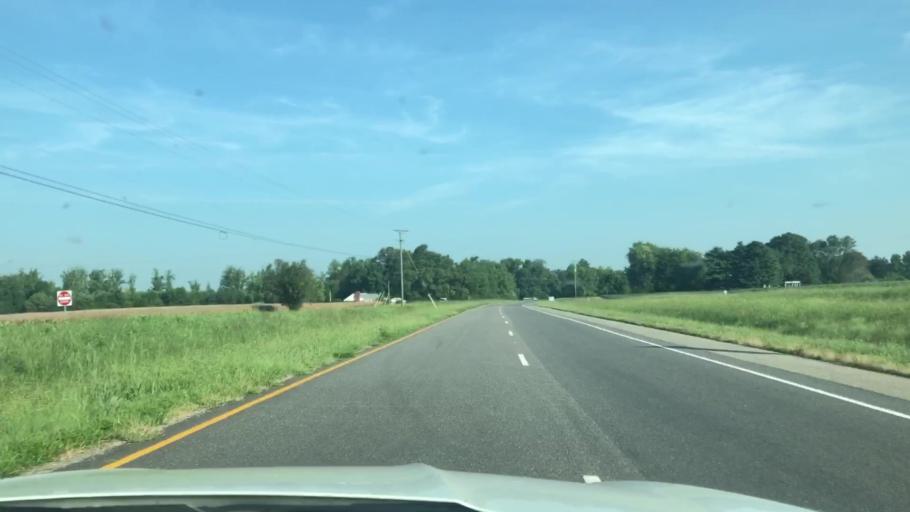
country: US
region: Virginia
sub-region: Middlesex County
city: Saluda
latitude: 37.6781
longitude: -76.6805
